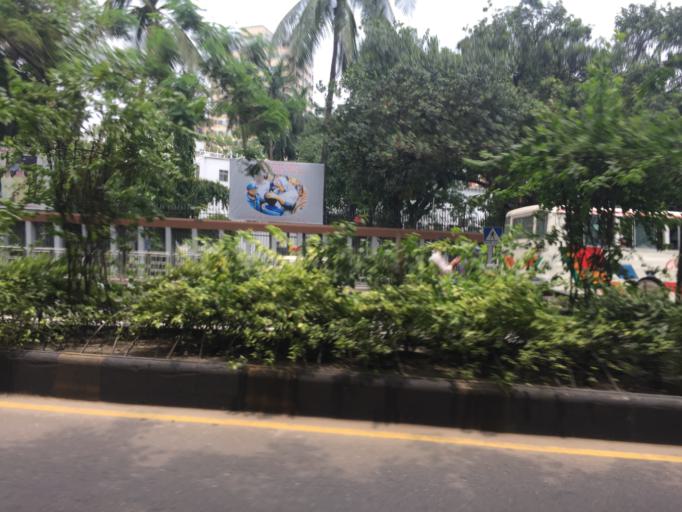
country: BD
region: Dhaka
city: Paltan
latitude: 23.7302
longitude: 90.4049
